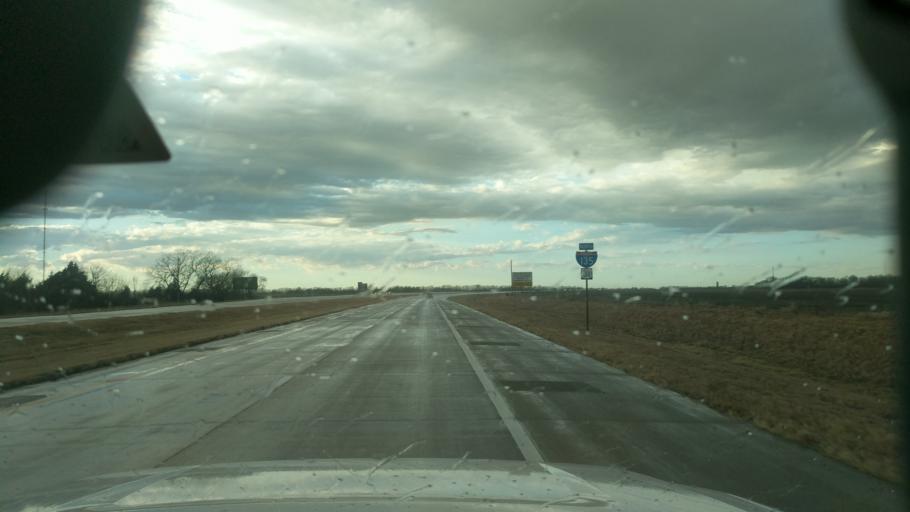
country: US
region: Kansas
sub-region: Harvey County
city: North Newton
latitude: 38.0875
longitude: -97.3529
